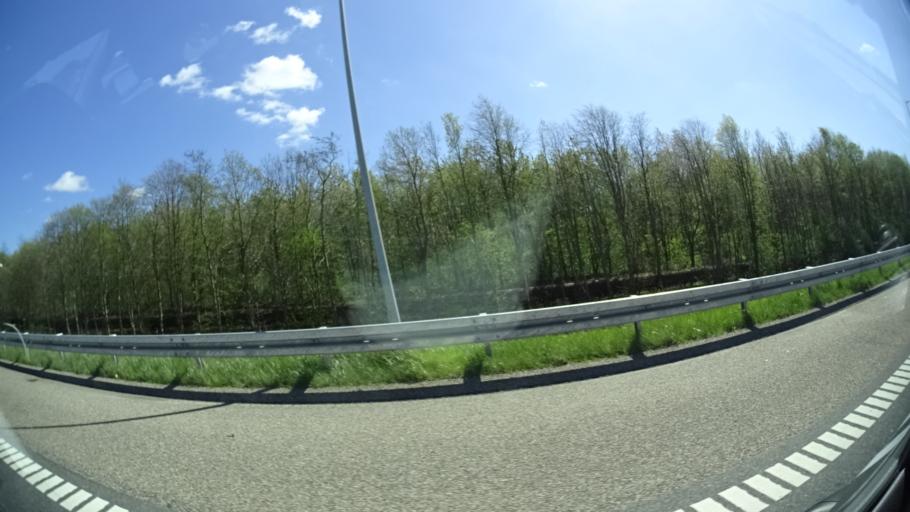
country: DK
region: Central Jutland
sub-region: Arhus Kommune
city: Stavtrup
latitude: 56.1347
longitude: 10.1492
